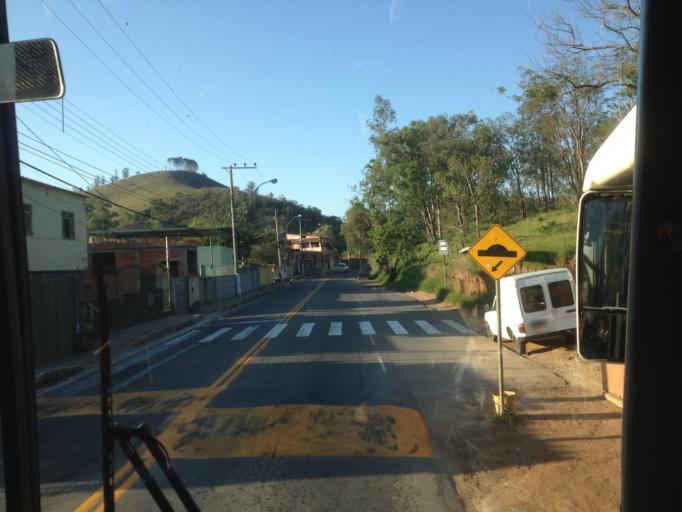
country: BR
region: Minas Gerais
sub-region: Juiz De Fora
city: Juiz de Fora
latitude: -21.6808
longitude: -43.3468
